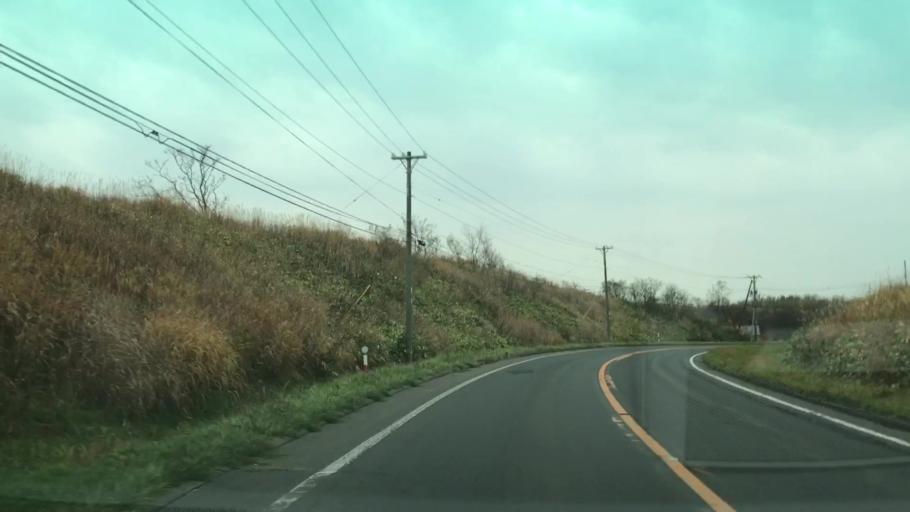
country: JP
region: Hokkaido
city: Ishikari
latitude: 43.3853
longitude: 141.4329
